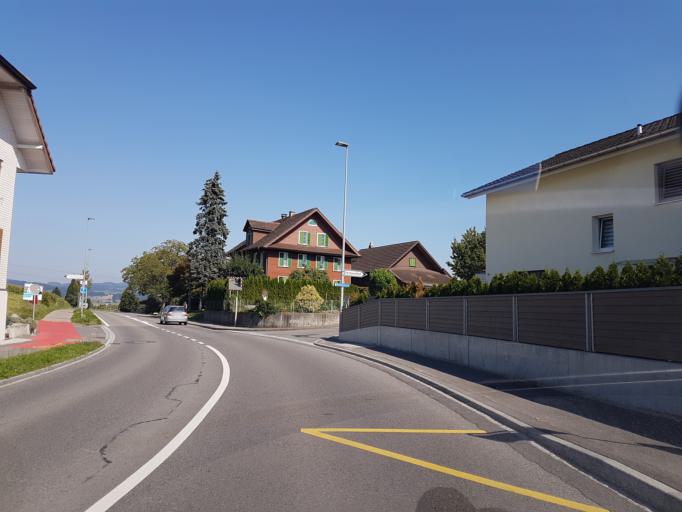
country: CH
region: Aargau
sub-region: Bezirk Muri
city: Muri
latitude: 47.2767
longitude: 8.3499
